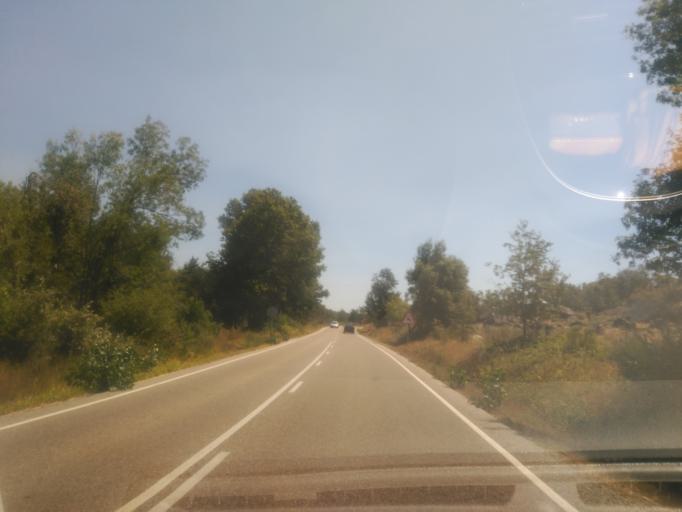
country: ES
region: Castille and Leon
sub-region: Provincia de Zamora
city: Galende
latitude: 42.1140
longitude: -6.6843
